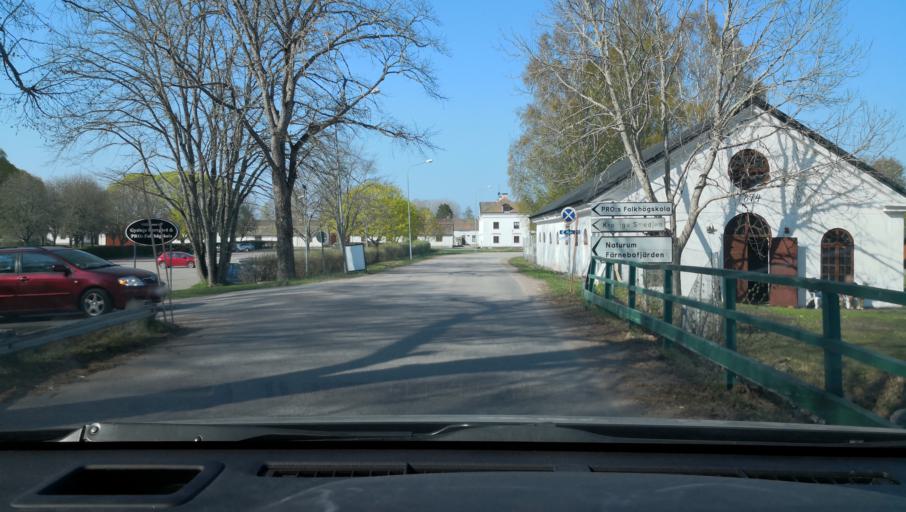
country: SE
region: Uppsala
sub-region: Heby Kommun
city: Tarnsjo
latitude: 60.2875
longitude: 16.8844
